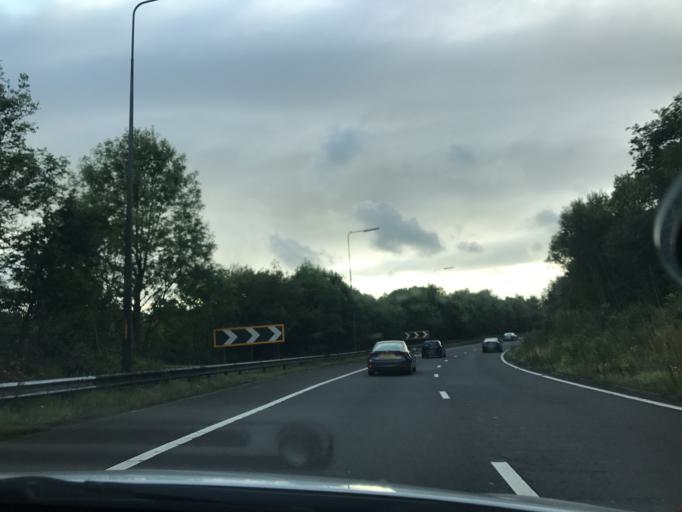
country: GB
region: England
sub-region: Cheshire West and Chester
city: Ledsham
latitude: 53.3018
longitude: -2.9696
